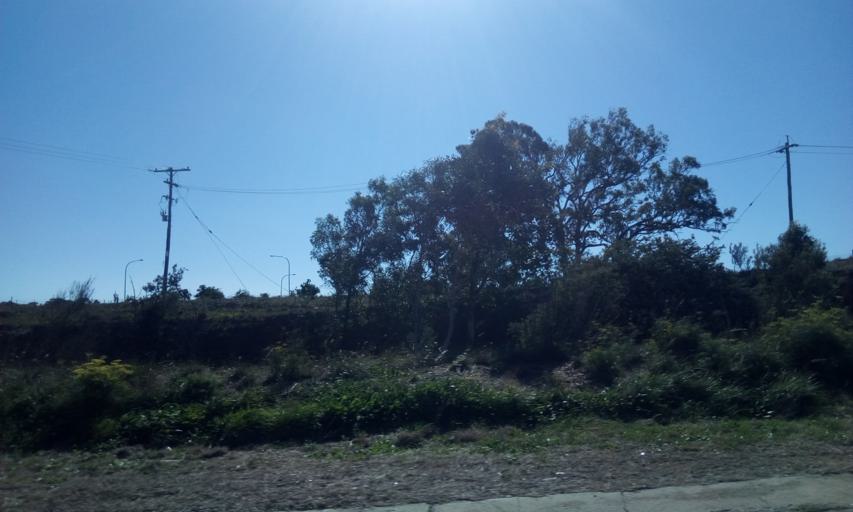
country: AU
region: New South Wales
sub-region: Goulburn Mulwaree
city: Goulburn
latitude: -34.7778
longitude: 149.6796
